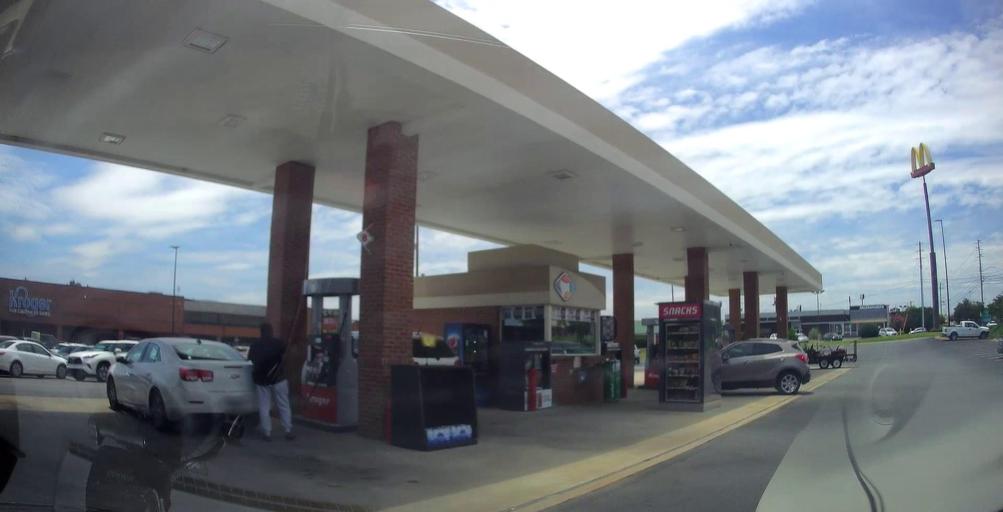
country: US
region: Georgia
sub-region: Houston County
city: Perry
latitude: 32.4677
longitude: -83.7403
